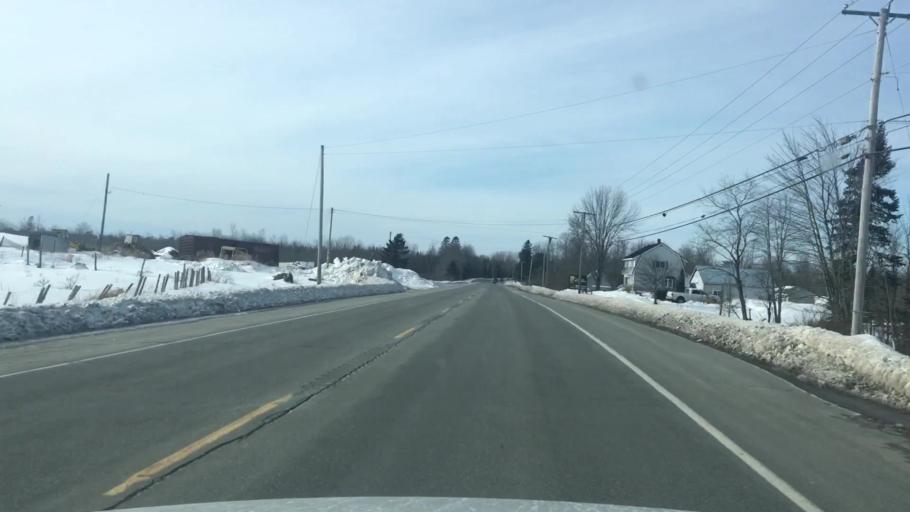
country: US
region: Maine
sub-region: Penobscot County
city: Kenduskeag
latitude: 44.9046
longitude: -68.8895
